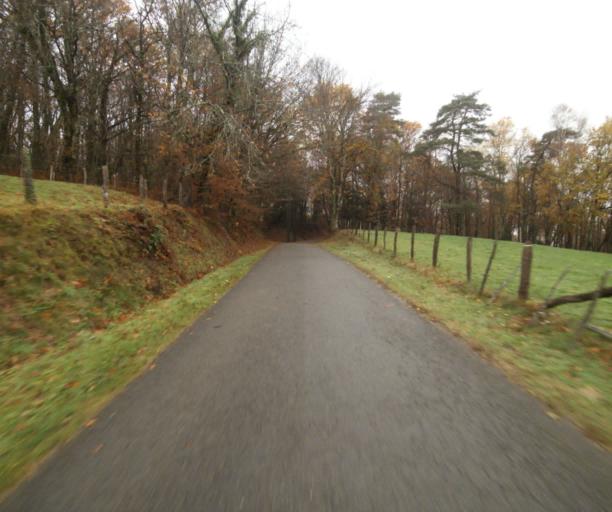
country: FR
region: Limousin
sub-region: Departement de la Correze
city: Cornil
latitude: 45.1980
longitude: 1.6419
